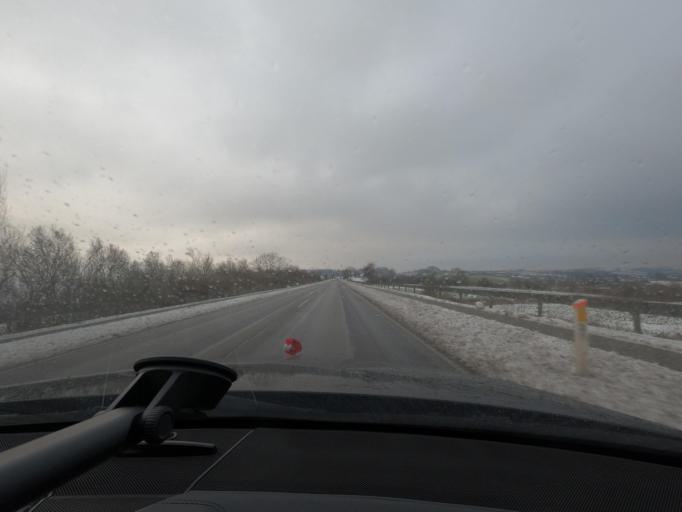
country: DK
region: South Denmark
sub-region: Sonderborg Kommune
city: Broager
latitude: 54.8999
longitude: 9.6850
